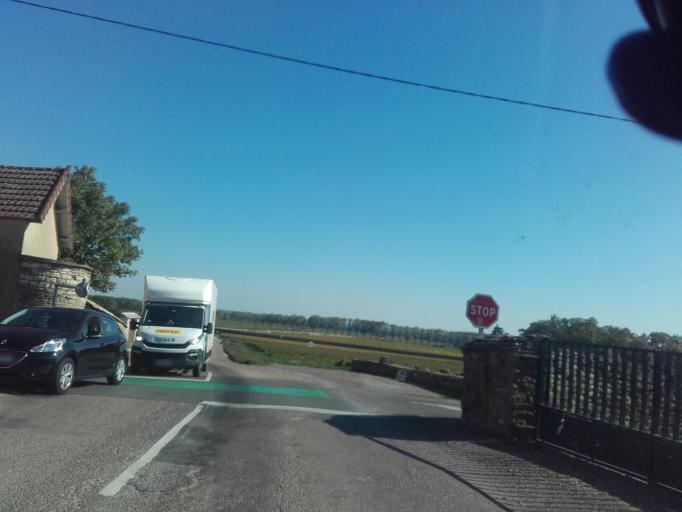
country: FR
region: Bourgogne
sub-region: Departement de la Cote-d'Or
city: Bligny-les-Beaune
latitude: 47.0124
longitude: 4.7976
